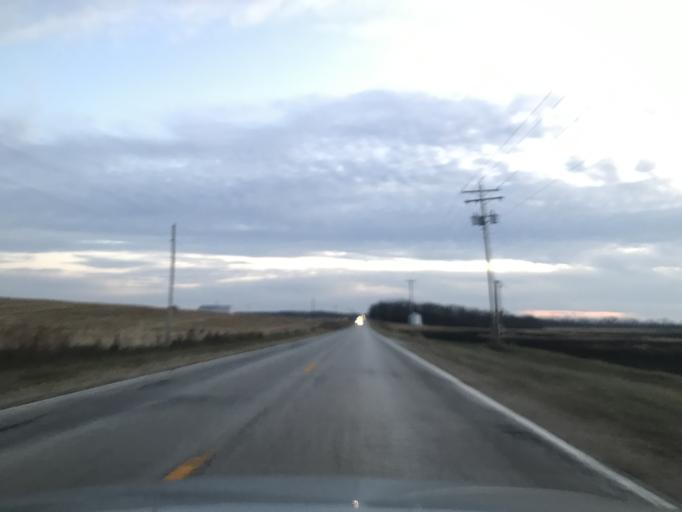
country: US
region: Iowa
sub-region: Des Moines County
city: Burlington
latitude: 40.6988
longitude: -91.0702
